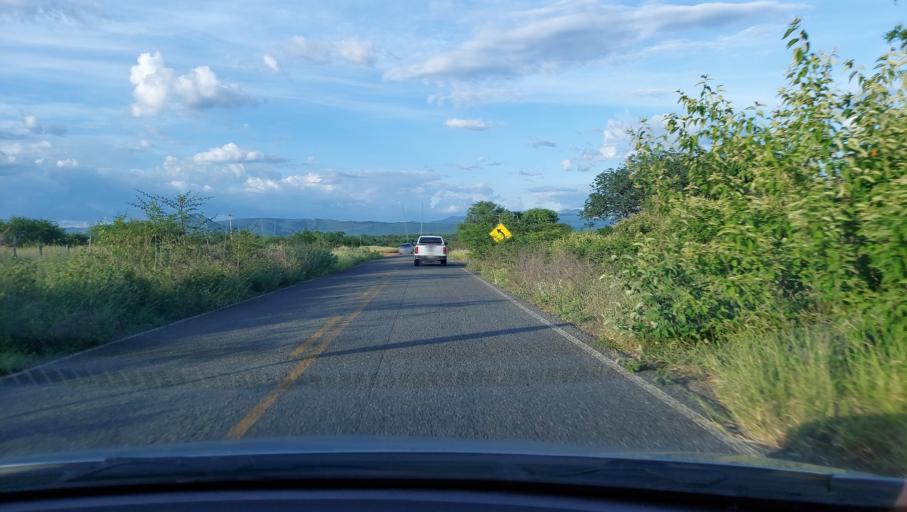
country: BR
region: Bahia
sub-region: Oliveira Dos Brejinhos
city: Beira Rio
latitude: -12.1987
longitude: -42.5383
